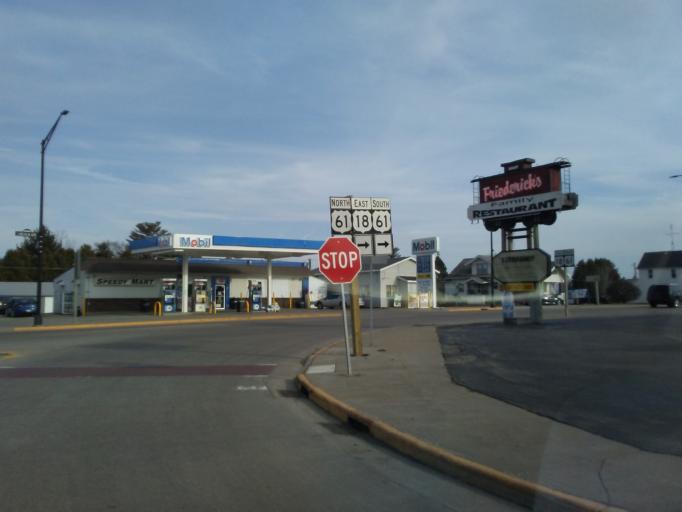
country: US
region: Wisconsin
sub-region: Grant County
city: Fennimore
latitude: 42.9883
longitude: -90.6559
